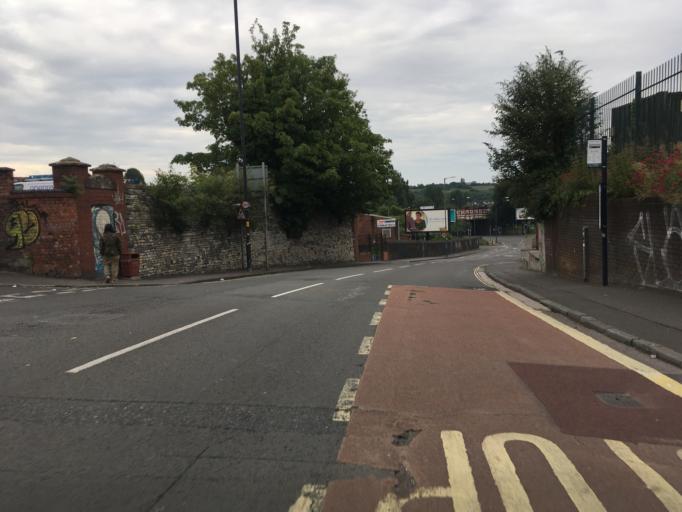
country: GB
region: England
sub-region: Bristol
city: Bristol
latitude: 51.4391
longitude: -2.6005
